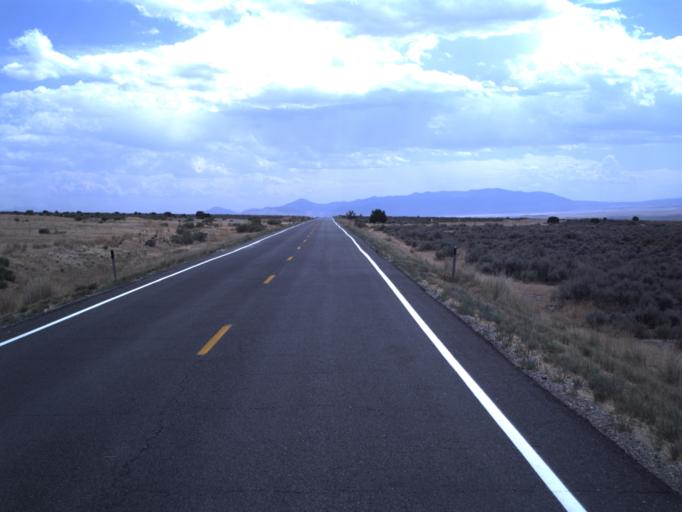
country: US
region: Utah
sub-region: Tooele County
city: Tooele
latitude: 40.3072
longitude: -112.2797
